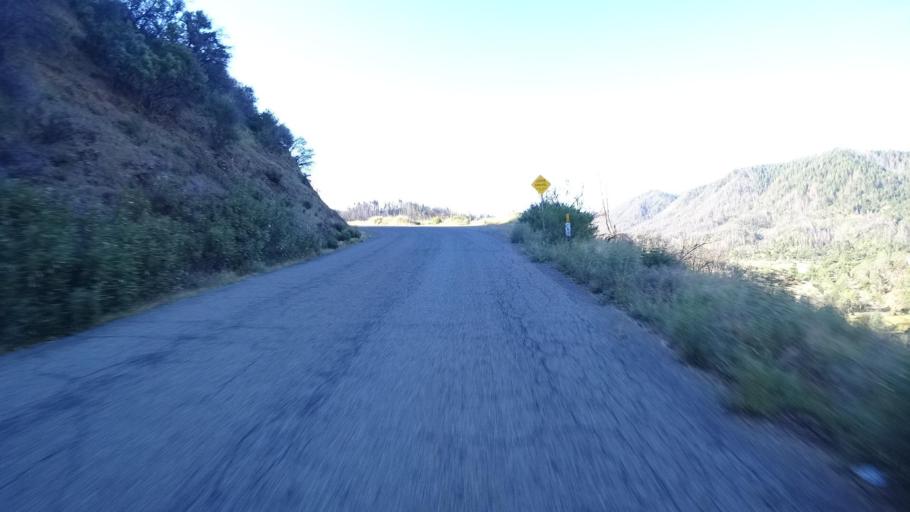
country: US
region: California
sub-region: Lake County
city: Upper Lake
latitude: 39.2585
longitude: -122.9453
